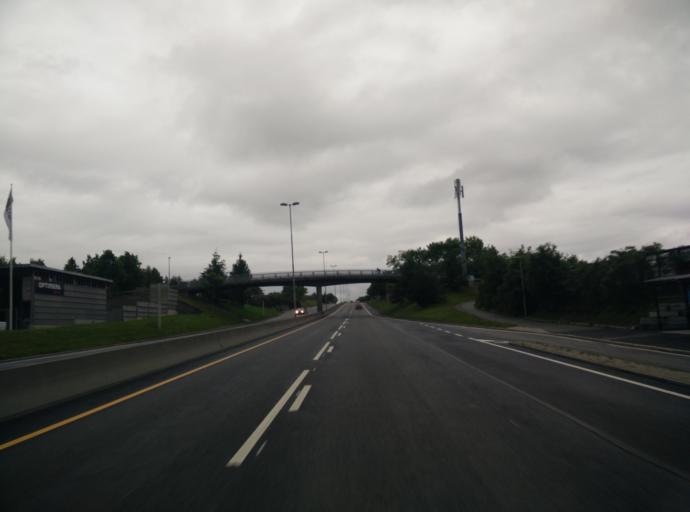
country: NO
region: Sor-Trondelag
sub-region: Trondheim
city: Trondheim
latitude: 63.4185
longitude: 10.4599
